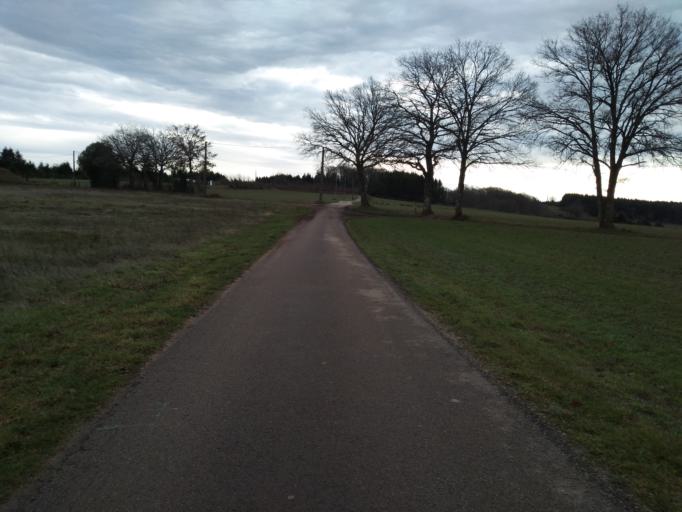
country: FR
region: Bourgogne
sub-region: Departement de la Cote-d'Or
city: Saulieu
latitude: 47.2789
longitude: 4.1534
